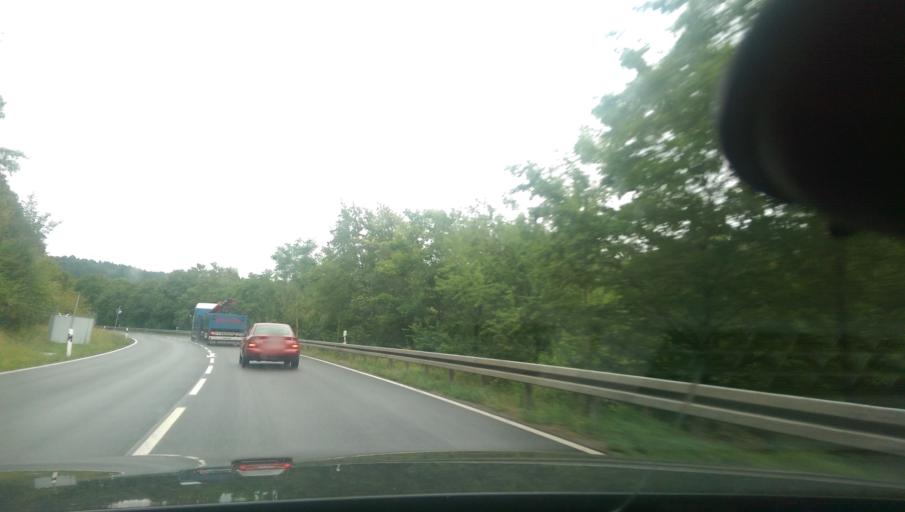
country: DE
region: Hesse
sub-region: Regierungsbezirk Kassel
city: Grossalmerode
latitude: 51.2620
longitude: 9.8326
